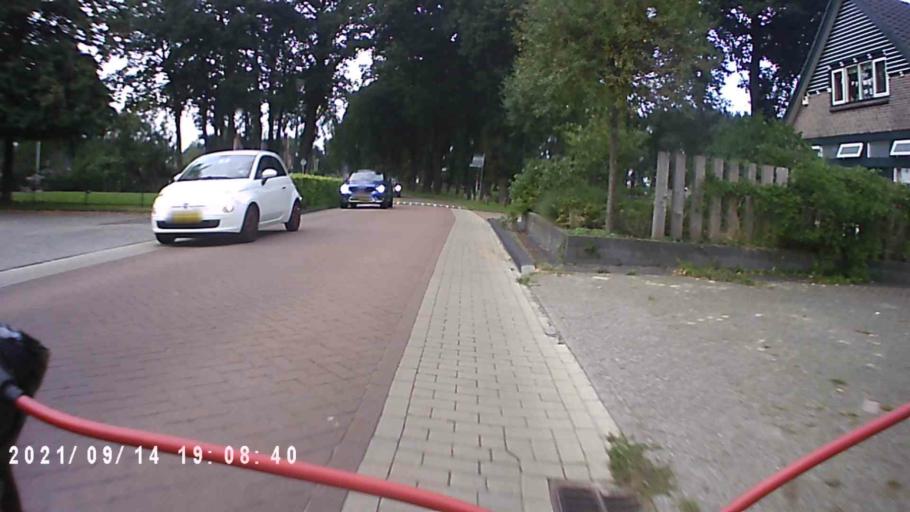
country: NL
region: Drenthe
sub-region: Gemeente Aa en Hunze
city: Anloo
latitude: 53.0551
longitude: 6.7273
